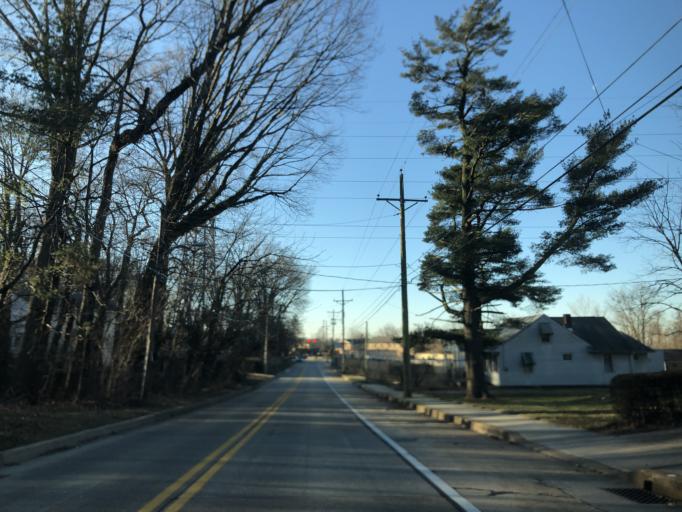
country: US
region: Delaware
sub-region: New Castle County
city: Bellefonte
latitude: 39.7623
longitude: -75.5106
